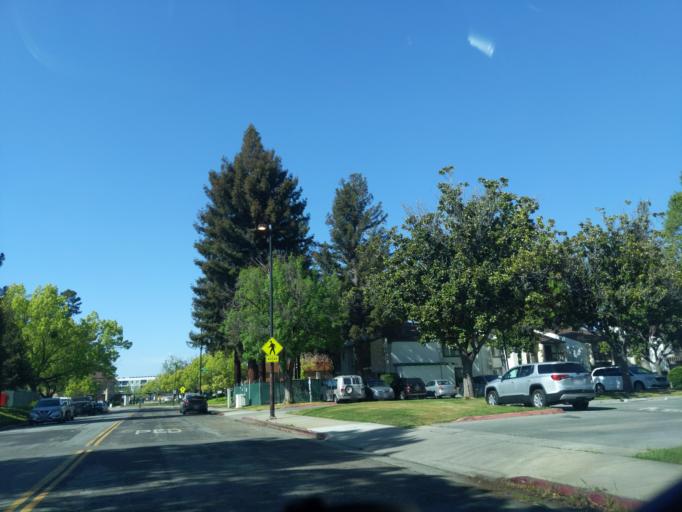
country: US
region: California
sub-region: Santa Clara County
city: Seven Trees
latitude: 37.2390
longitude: -121.7994
